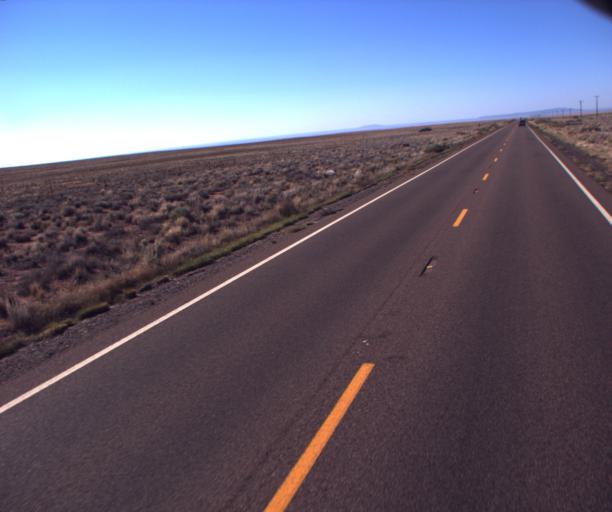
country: US
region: Arizona
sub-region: Navajo County
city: Winslow
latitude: 35.1145
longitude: -110.5168
